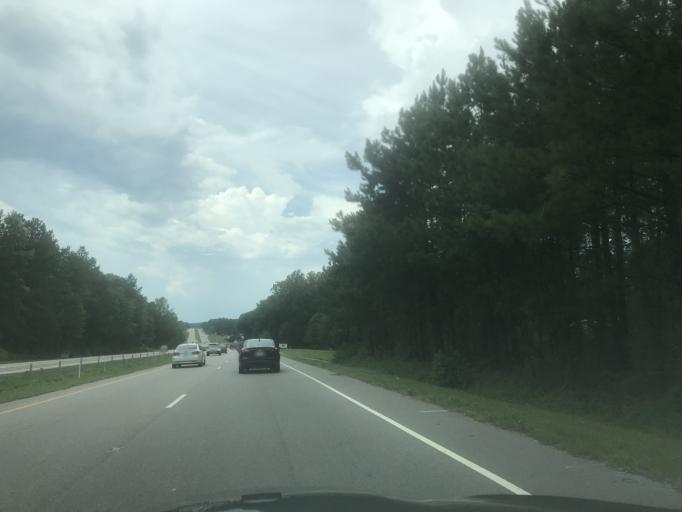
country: US
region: North Carolina
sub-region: Johnston County
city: Clayton
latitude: 35.6822
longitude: -78.5339
